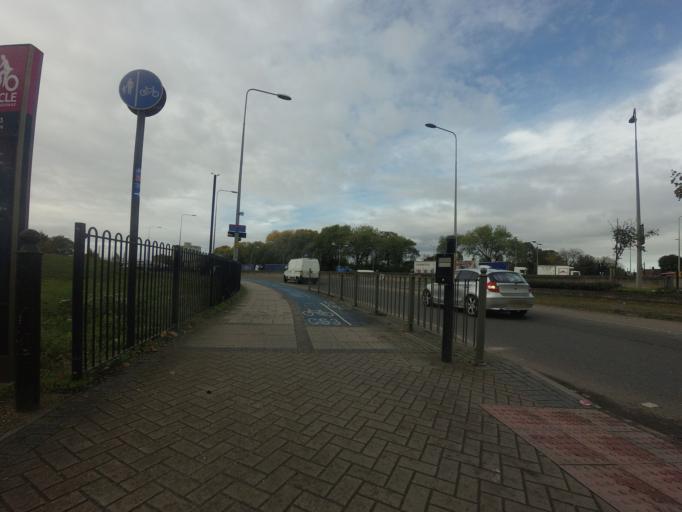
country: GB
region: England
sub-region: Greater London
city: Barking
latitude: 51.5295
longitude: 0.0928
